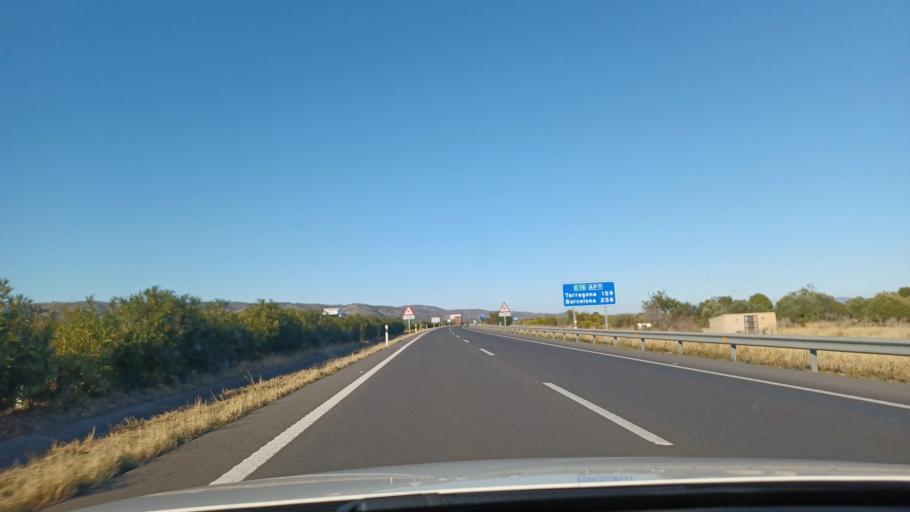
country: ES
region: Valencia
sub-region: Provincia de Castello
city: Orpesa/Oropesa del Mar
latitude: 40.1121
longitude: 0.1313
